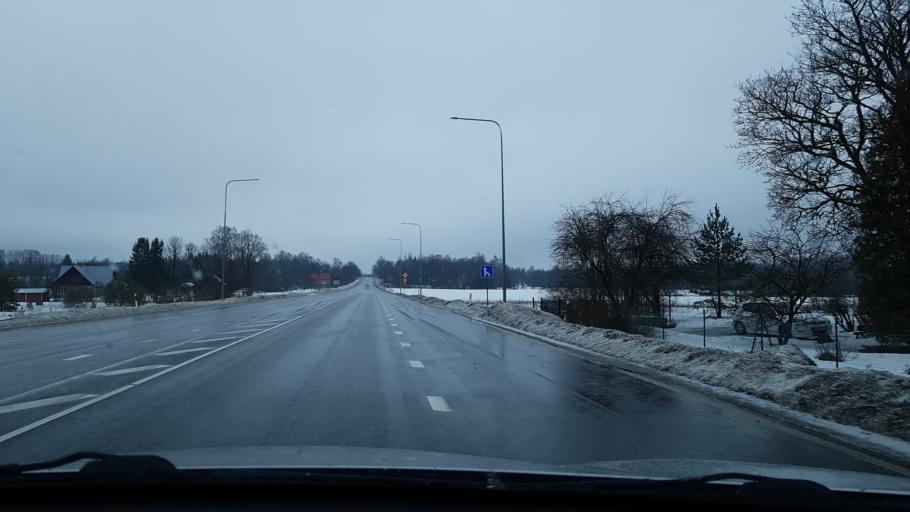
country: EE
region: Raplamaa
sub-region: Kohila vald
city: Kohila
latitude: 59.0967
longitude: 24.8013
